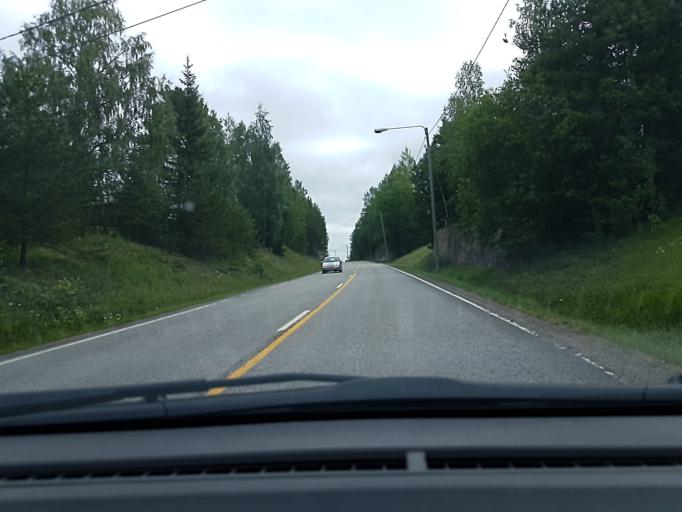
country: FI
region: Uusimaa
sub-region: Helsinki
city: Sibbo
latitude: 60.3630
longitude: 25.2186
